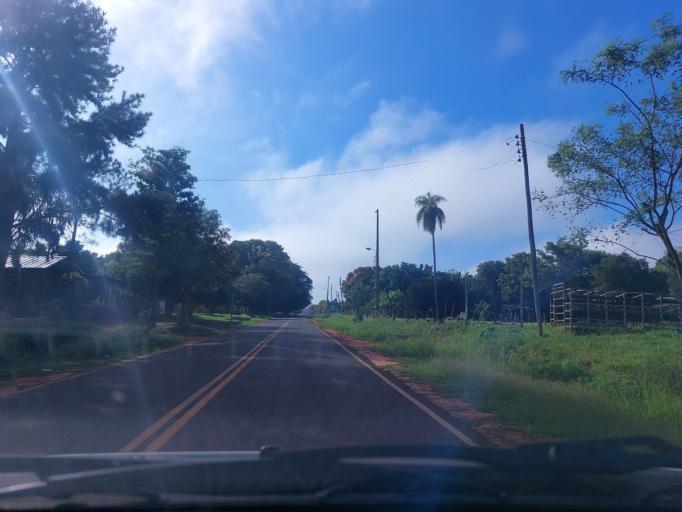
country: PY
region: San Pedro
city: Guayaybi
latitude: -24.5319
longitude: -56.5212
